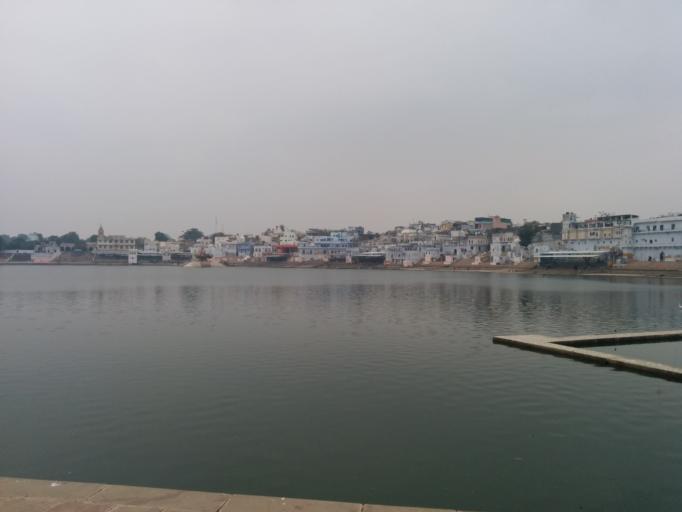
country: IN
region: Rajasthan
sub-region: Ajmer
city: Pushkar
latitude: 26.4882
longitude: 74.5562
